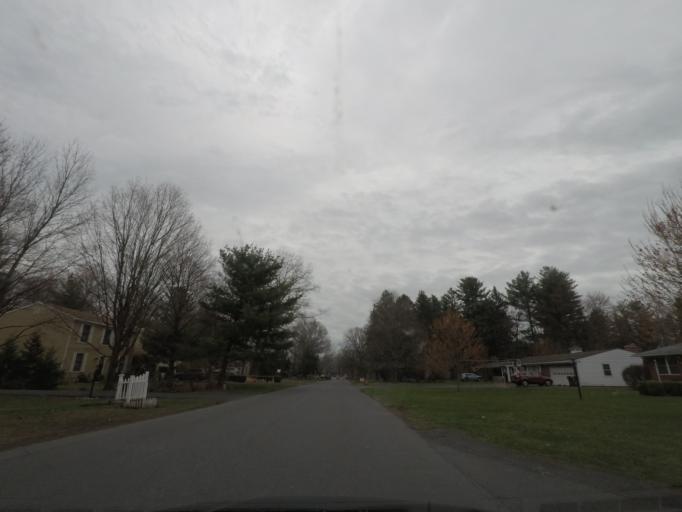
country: US
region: New York
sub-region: Albany County
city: Delmar
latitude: 42.6077
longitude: -73.8366
